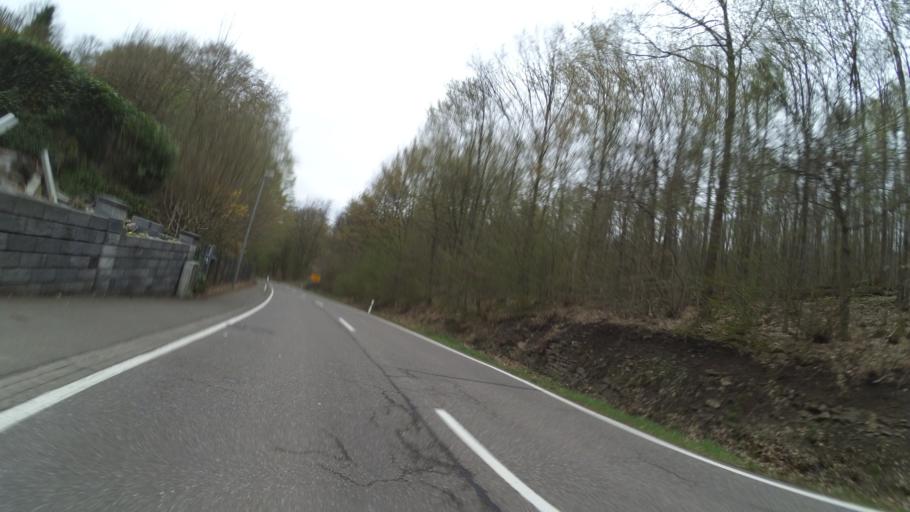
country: DE
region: Saarland
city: Sulzbach
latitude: 49.3023
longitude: 7.0813
